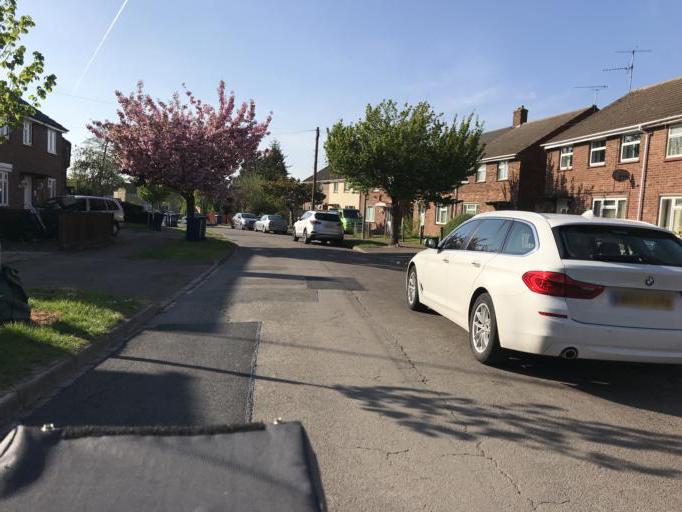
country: GB
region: England
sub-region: Cambridgeshire
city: Cambridge
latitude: 52.1821
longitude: 0.1594
